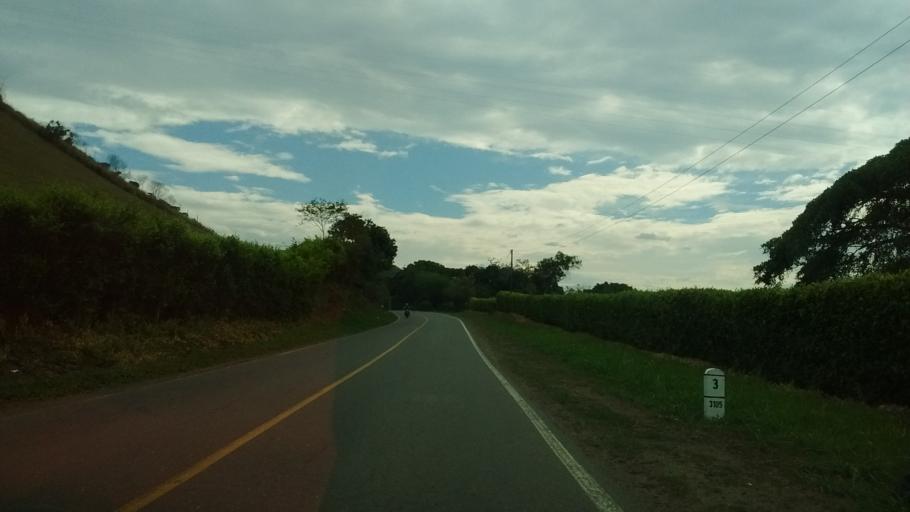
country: CO
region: Cauca
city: Santander de Quilichao
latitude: 3.0375
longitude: -76.4658
